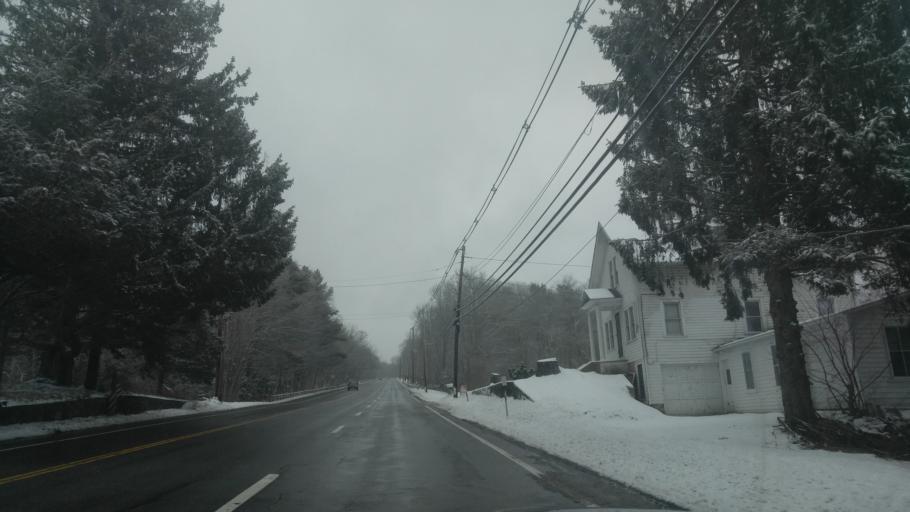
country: US
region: Rhode Island
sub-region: Providence County
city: Foster
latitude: 41.8221
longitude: -71.6991
